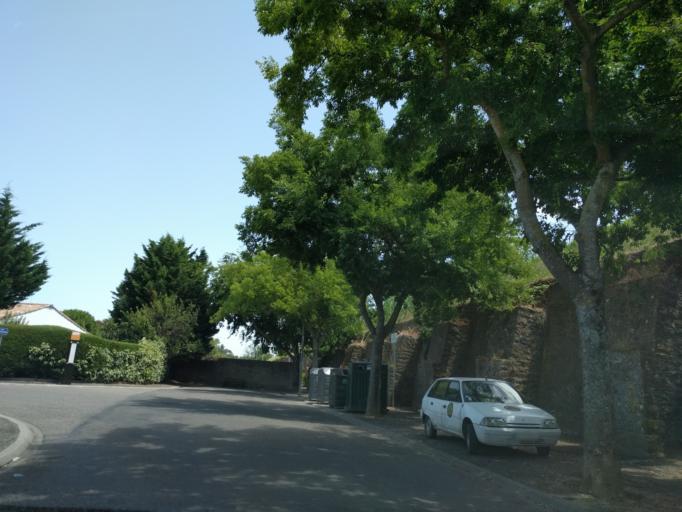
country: FR
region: Languedoc-Roussillon
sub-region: Departement de l'Aude
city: Carcassonne
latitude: 43.2188
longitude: 2.3578
